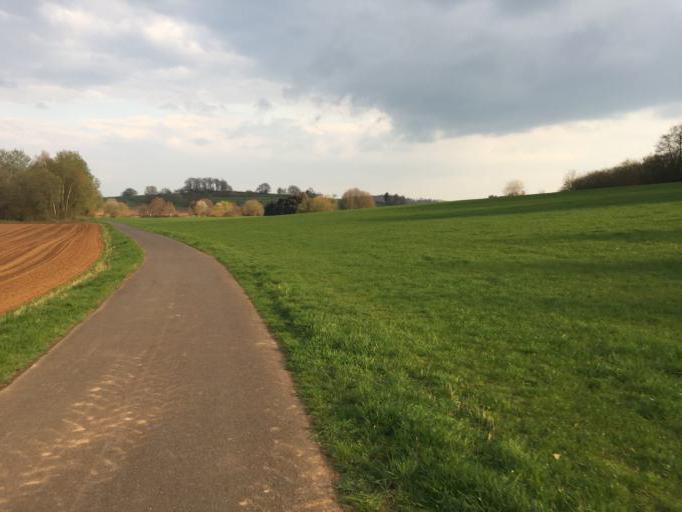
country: DE
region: Hesse
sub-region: Regierungsbezirk Giessen
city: Laubach
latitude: 50.5414
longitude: 8.9617
